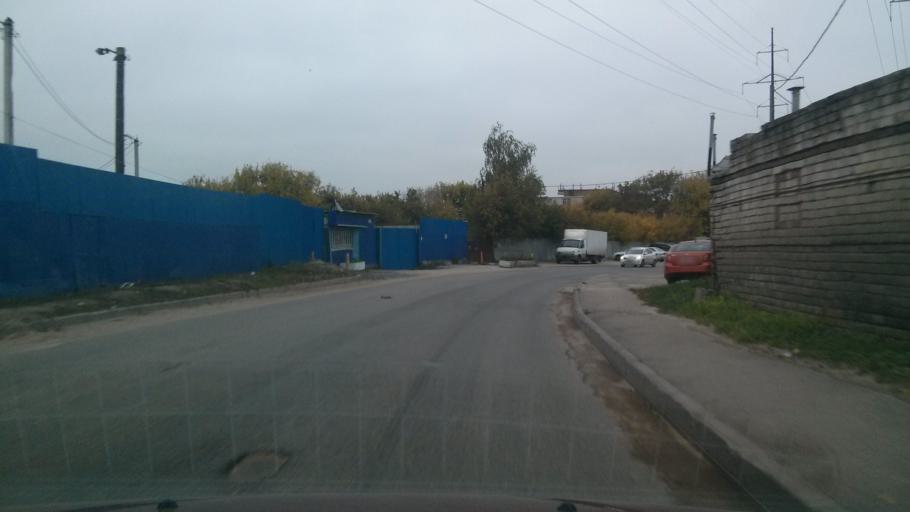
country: RU
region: Nizjnij Novgorod
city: Nizhniy Novgorod
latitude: 56.3076
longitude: 44.0101
